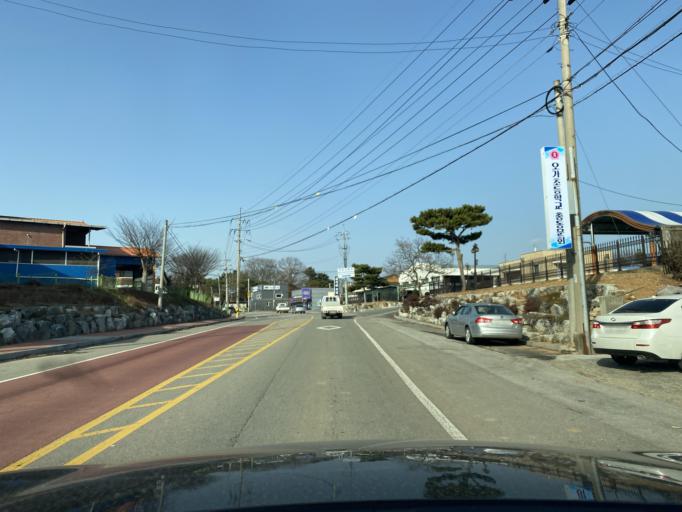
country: KR
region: Chungcheongnam-do
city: Yesan
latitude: 36.6878
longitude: 126.7982
